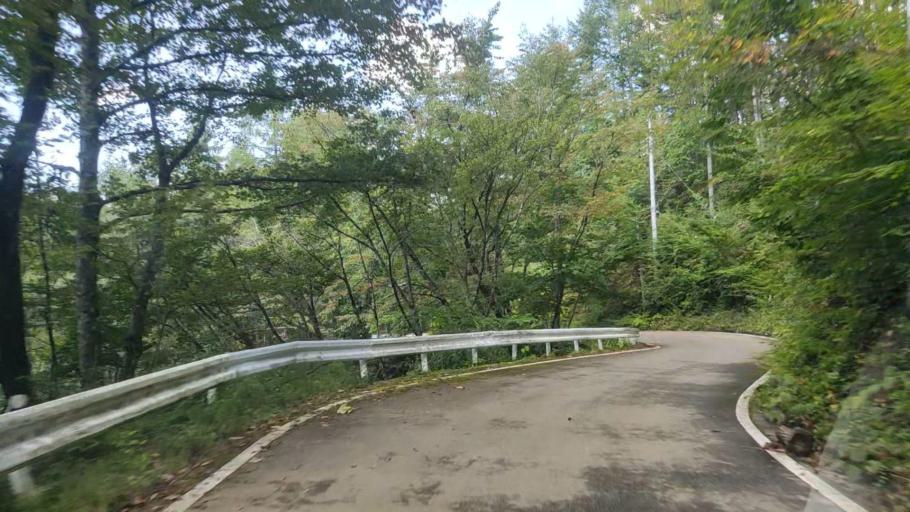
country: JP
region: Gunma
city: Nakanojomachi
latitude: 36.6483
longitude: 138.6196
